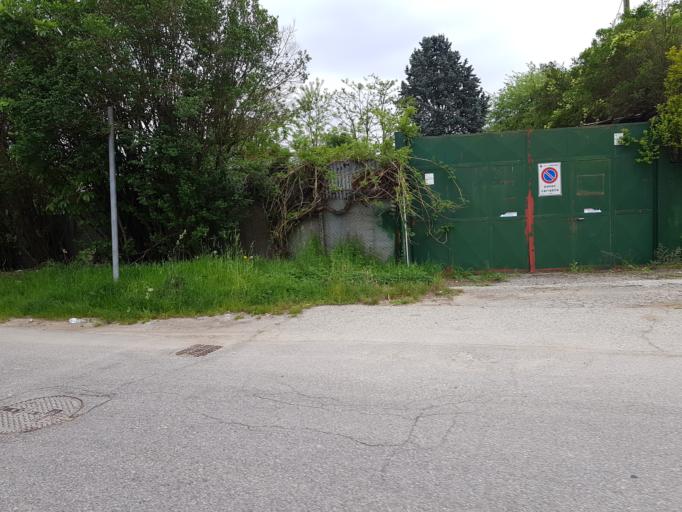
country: IT
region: Piedmont
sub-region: Provincia di Torino
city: Lesna
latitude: 45.0576
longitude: 7.6078
